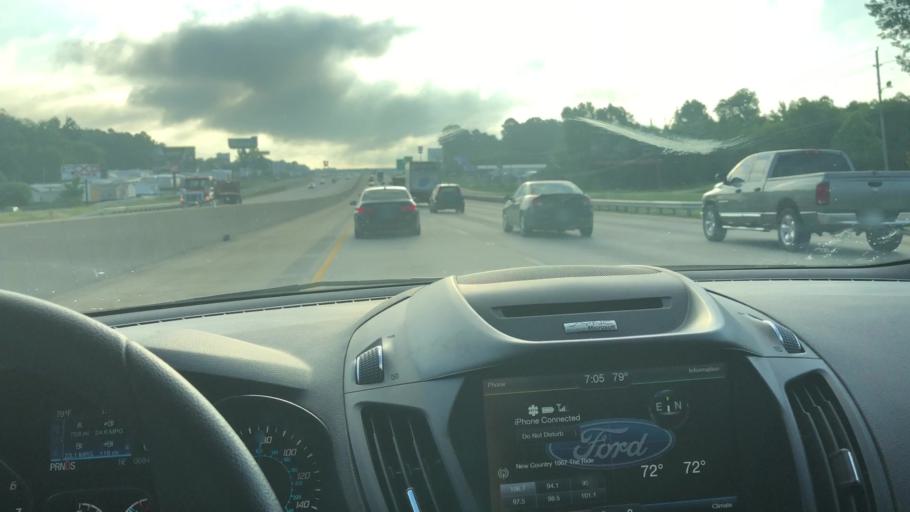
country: US
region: Arkansas
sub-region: Pulaski County
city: Alexander
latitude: 34.6372
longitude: -92.4537
